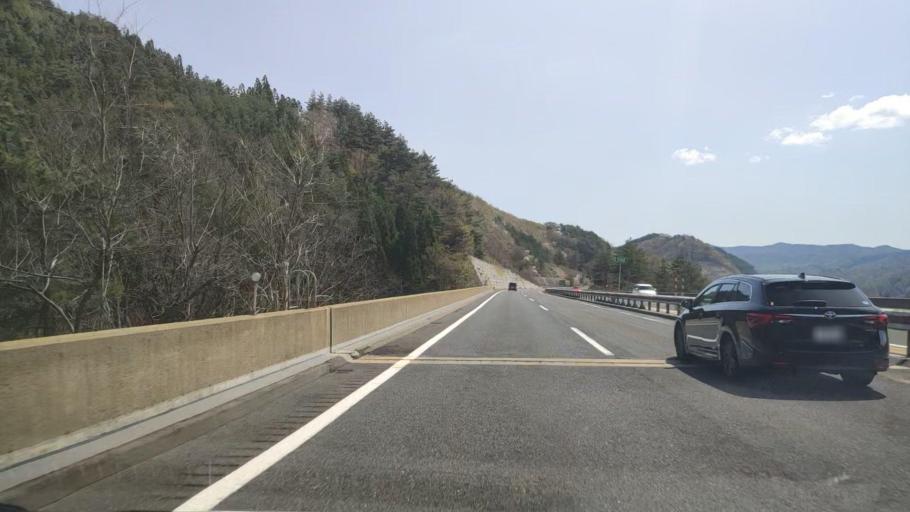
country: JP
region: Iwate
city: Ichinohe
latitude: 40.2297
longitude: 141.3173
